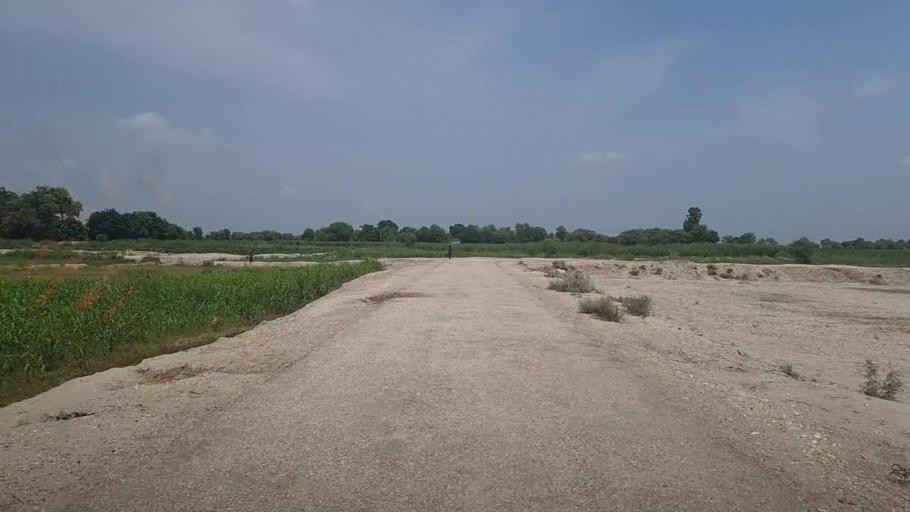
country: PK
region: Sindh
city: Ubauro
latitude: 28.2437
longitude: 69.8269
